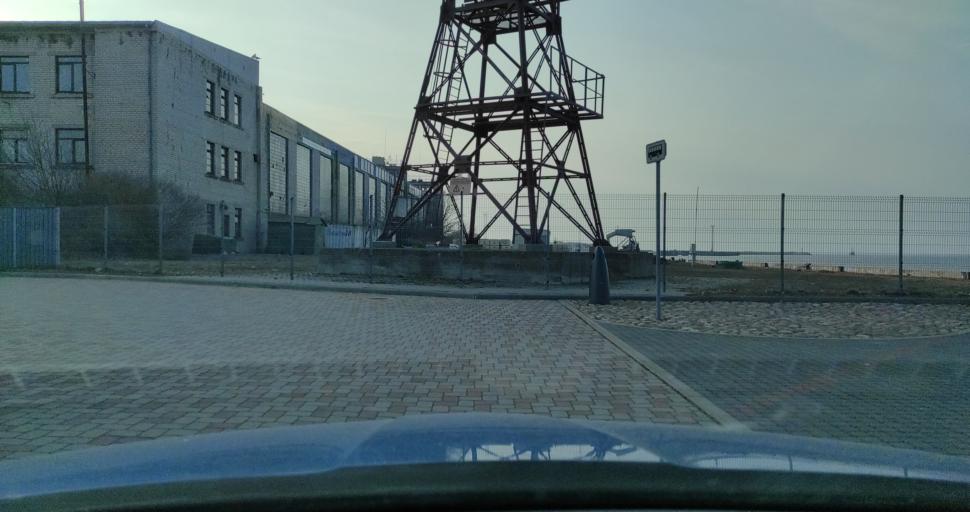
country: LV
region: Ventspils
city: Ventspils
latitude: 57.3946
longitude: 21.5425
